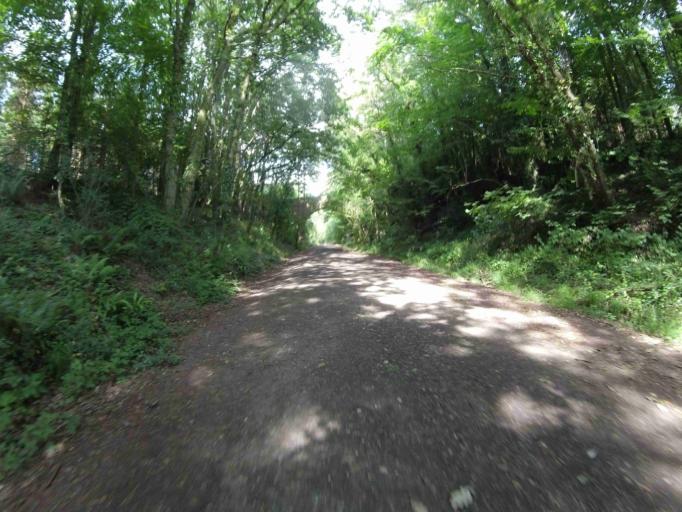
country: GB
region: England
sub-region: Devon
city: Budleigh Salterton
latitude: 50.6320
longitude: -3.3551
